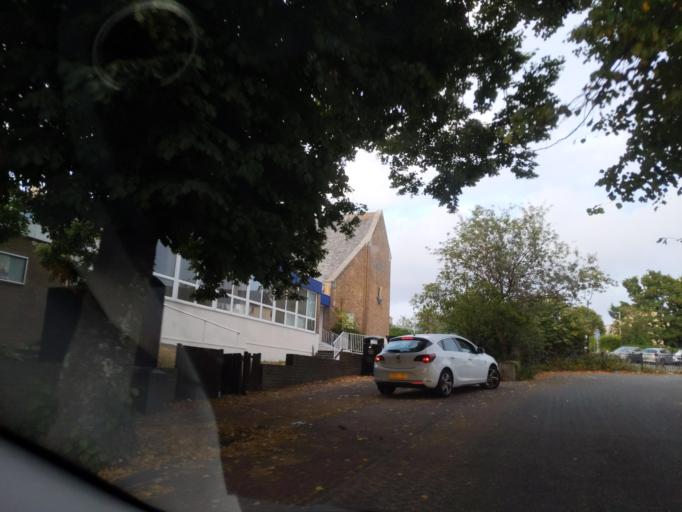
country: GB
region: England
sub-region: Cornwall
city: Millbrook
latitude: 50.3803
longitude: -4.1761
